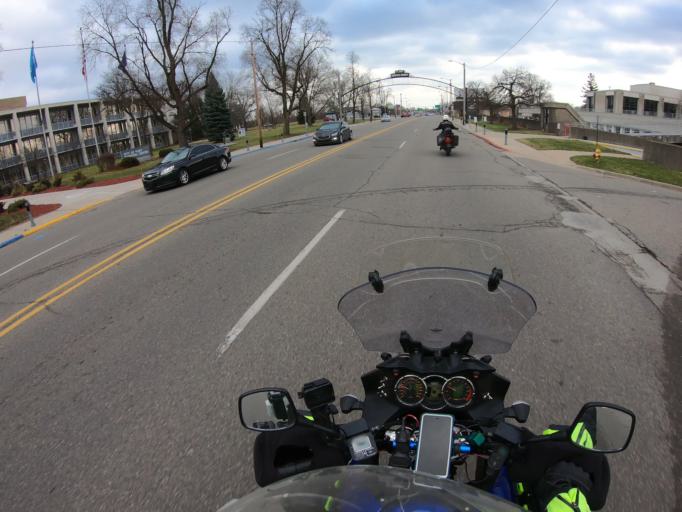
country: US
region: Michigan
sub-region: Genesee County
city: Flint
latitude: 43.0101
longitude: -83.6852
